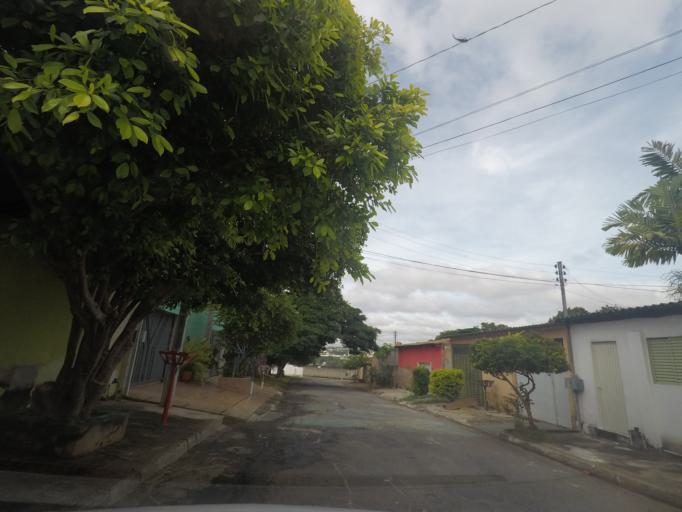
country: BR
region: Goias
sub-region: Goiania
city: Goiania
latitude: -16.6619
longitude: -49.1966
